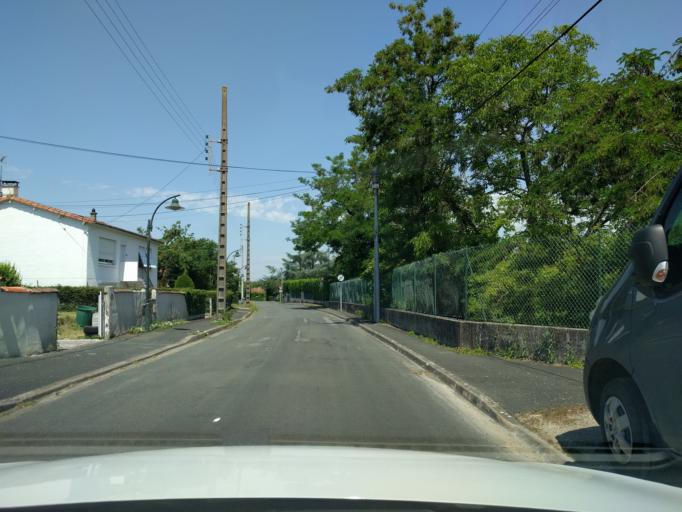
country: FR
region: Poitou-Charentes
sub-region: Departement des Deux-Sevres
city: Niort
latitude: 46.3402
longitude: -0.4781
